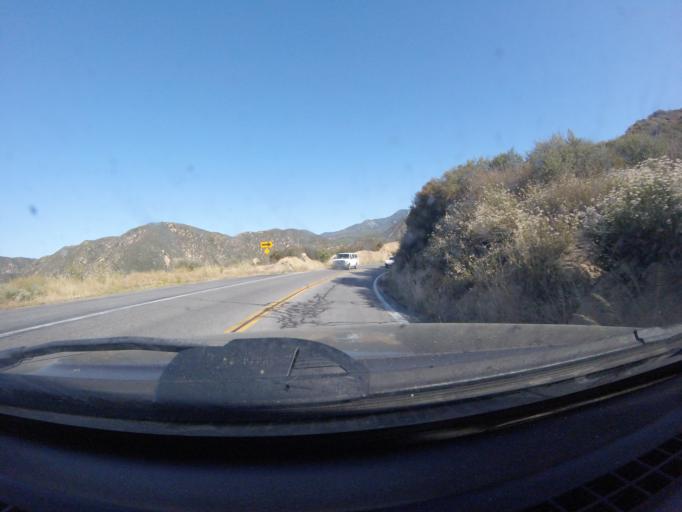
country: US
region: California
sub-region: San Bernardino County
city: Highland
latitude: 34.1837
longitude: -117.1761
